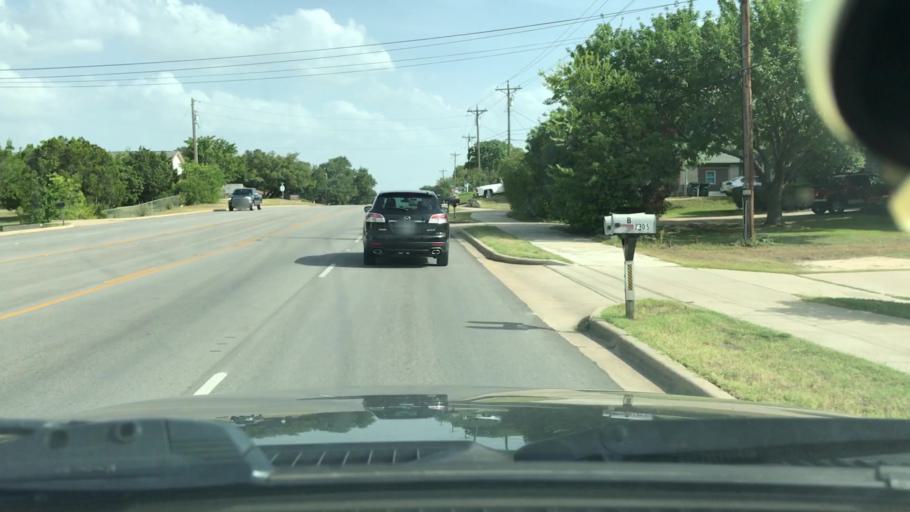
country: US
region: Texas
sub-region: Williamson County
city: Leander
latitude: 30.5451
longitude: -97.8514
